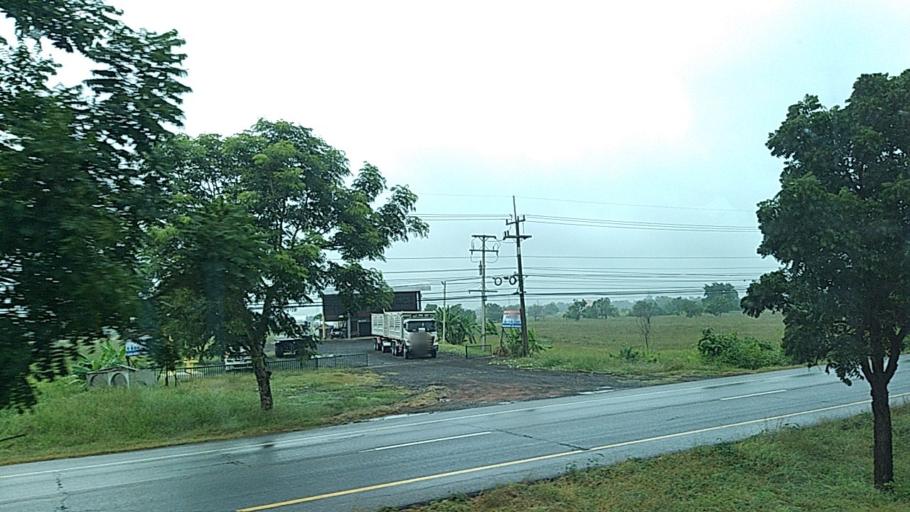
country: TH
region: Nakhon Ratchasima
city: Phimai
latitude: 15.2301
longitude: 102.3716
